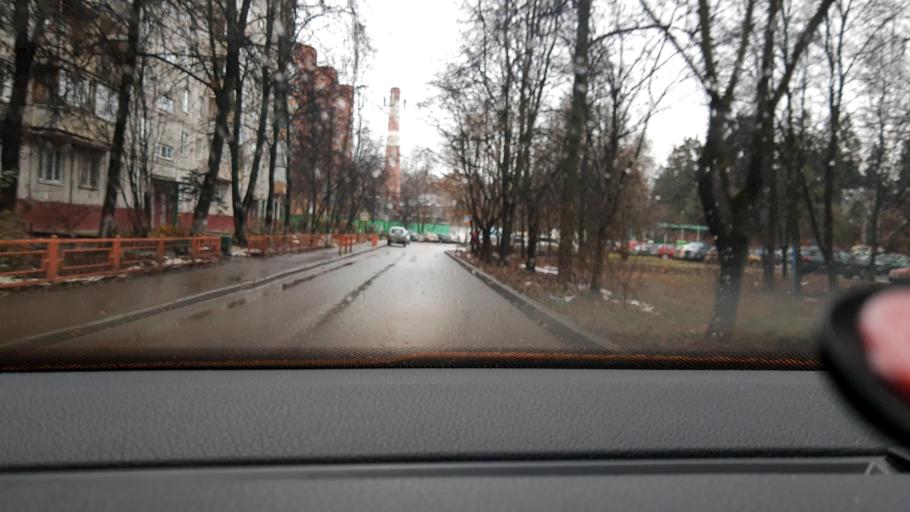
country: RU
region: Moskovskaya
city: Yubileyny
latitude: 55.9297
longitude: 37.8351
